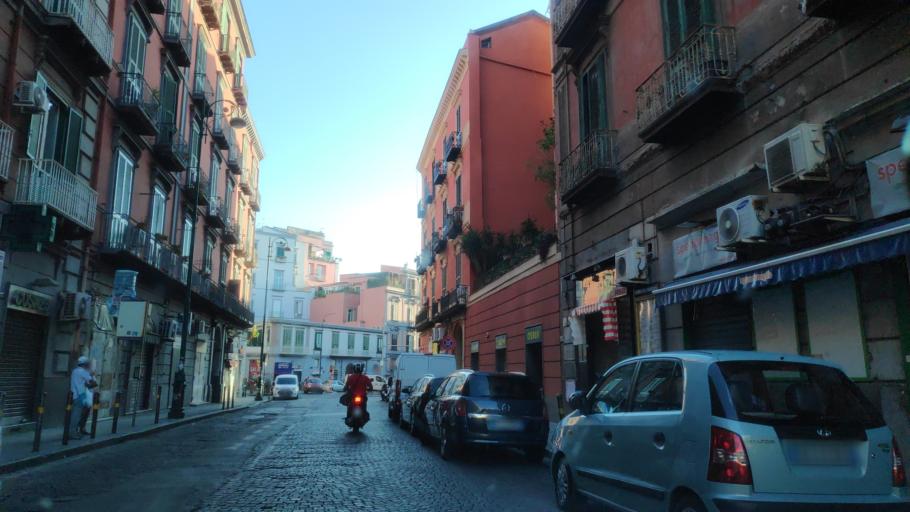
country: IT
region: Campania
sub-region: Provincia di Napoli
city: Napoli
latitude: 40.8508
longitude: 14.2421
